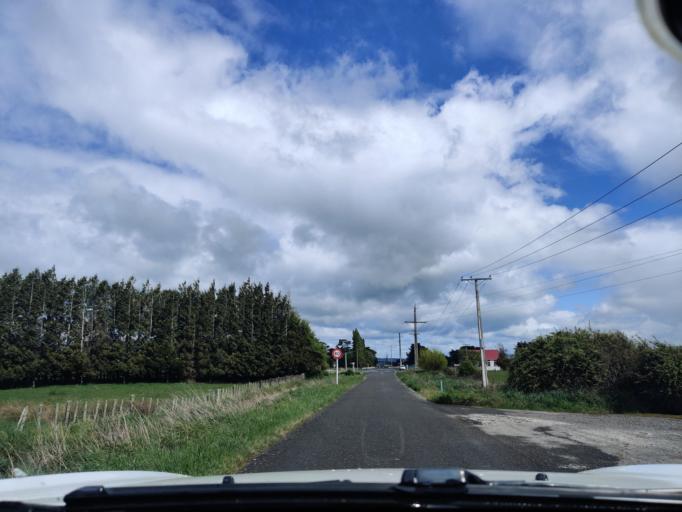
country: NZ
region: Manawatu-Wanganui
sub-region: Palmerston North City
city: Palmerston North
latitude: -40.3163
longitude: 175.8567
